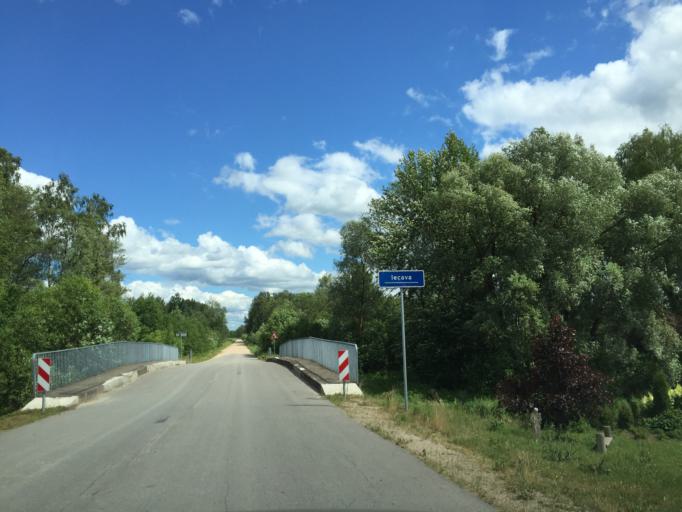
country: LV
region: Vecumnieki
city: Vecumnieki
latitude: 56.4680
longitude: 24.4444
